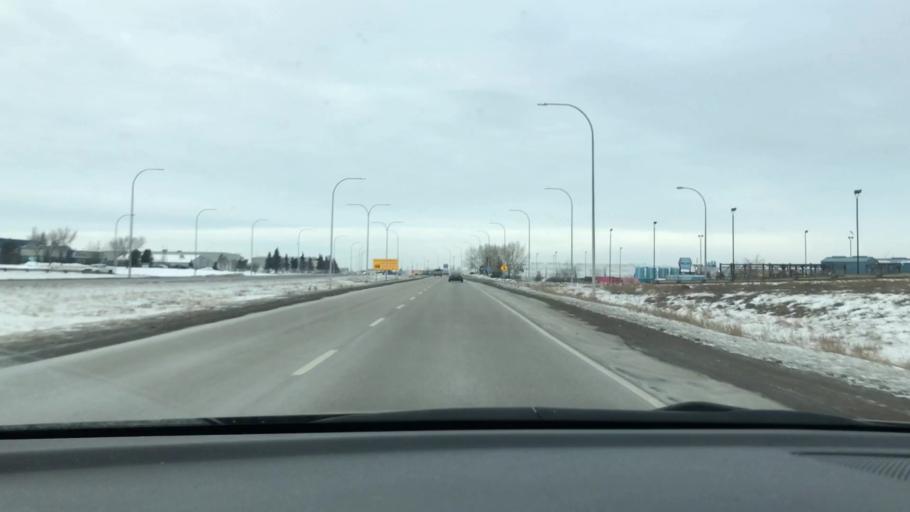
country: CA
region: Alberta
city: Sherwood Park
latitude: 53.5172
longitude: -113.3962
